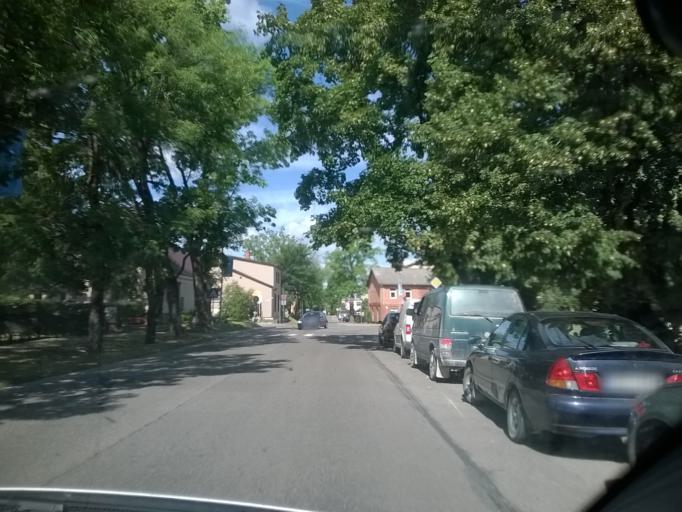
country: LV
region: Aluksnes Rajons
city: Aluksne
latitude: 57.4220
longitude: 27.0495
